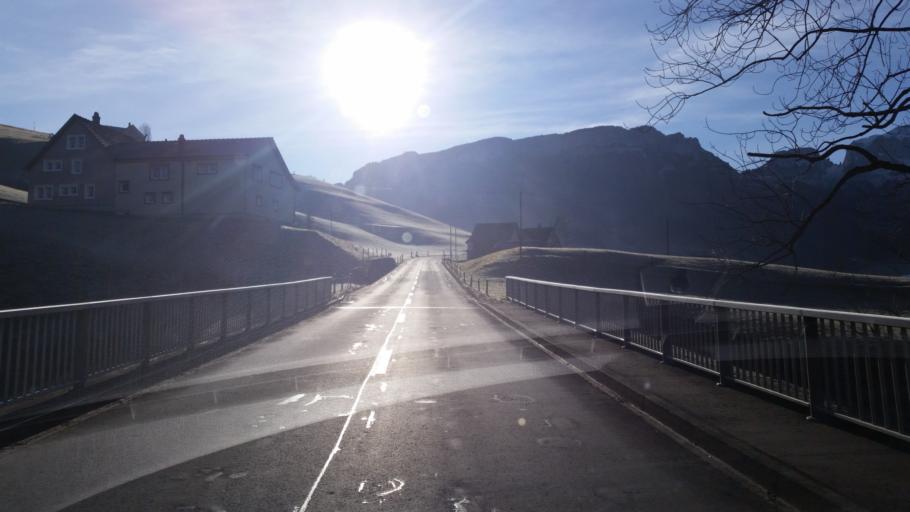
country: CH
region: Appenzell Innerrhoden
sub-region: Appenzell Inner Rhodes
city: Appenzell
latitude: 47.3154
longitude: 9.4377
